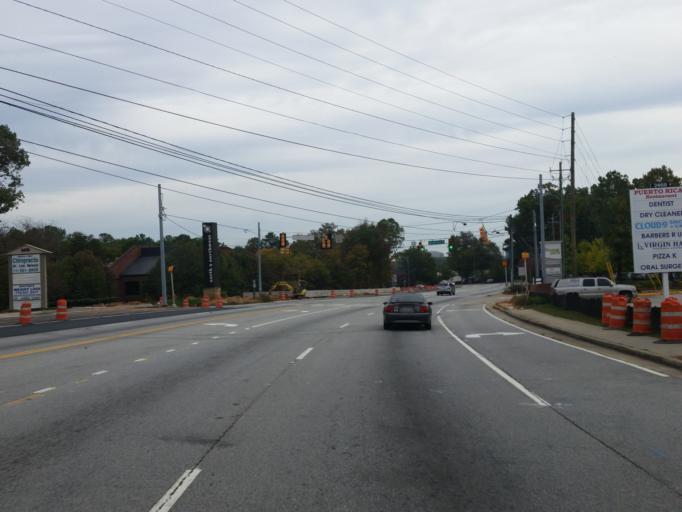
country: US
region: Georgia
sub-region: Cobb County
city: Smyrna
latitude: 33.9031
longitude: -84.4815
